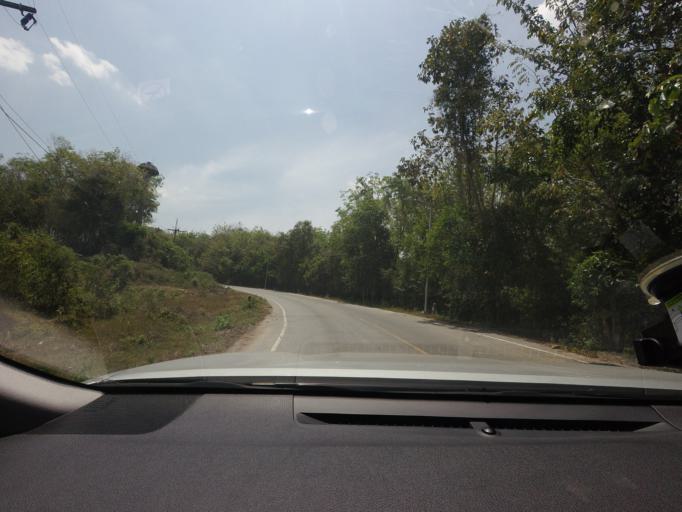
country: TH
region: Narathiwat
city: Rueso
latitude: 6.3898
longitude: 101.5023
